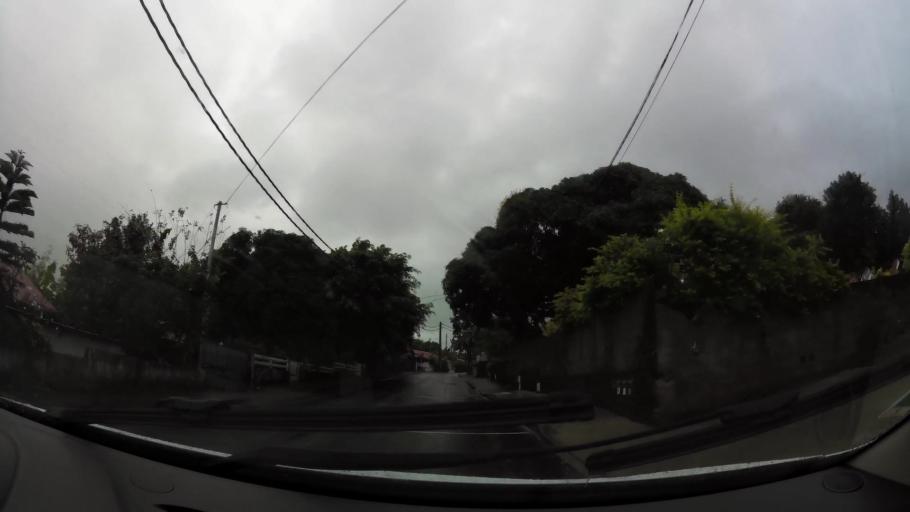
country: RE
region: Reunion
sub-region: Reunion
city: Saint-Benoit
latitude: -21.0221
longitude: 55.6990
